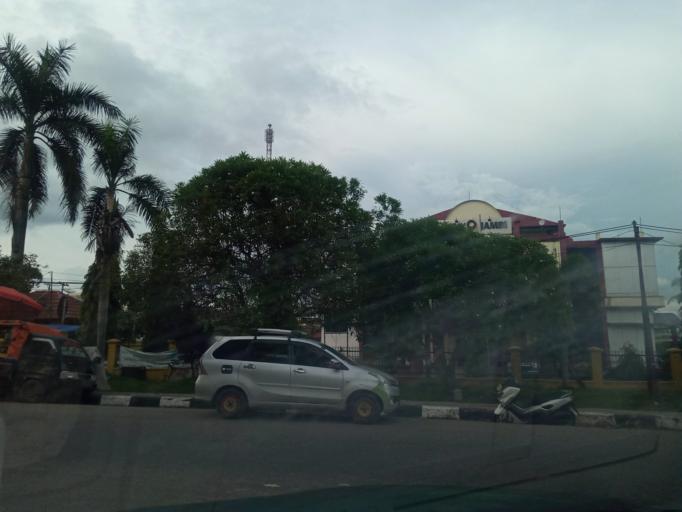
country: ID
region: Jambi
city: Sarolangun
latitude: -2.3021
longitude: 102.7246
